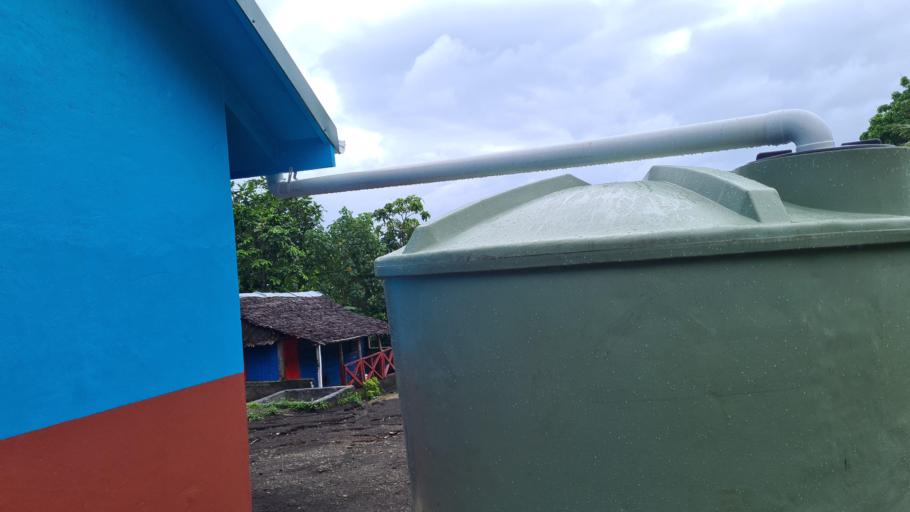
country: VU
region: Malampa
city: Lakatoro
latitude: -16.4650
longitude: 168.2507
